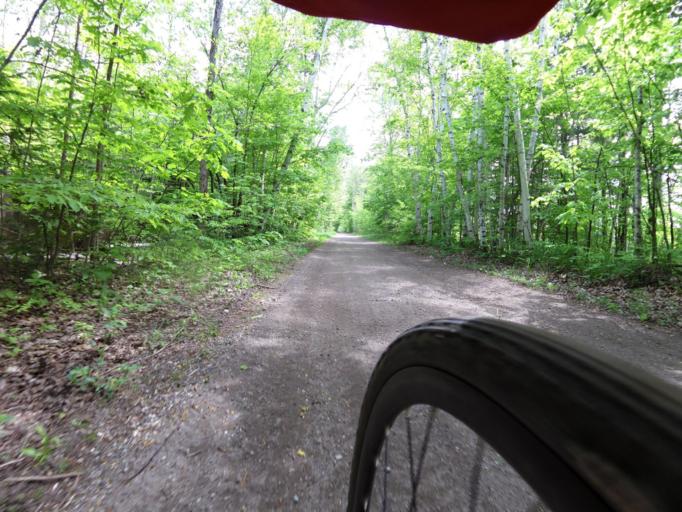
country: CA
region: Ontario
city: Renfrew
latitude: 45.2000
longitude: -76.6854
